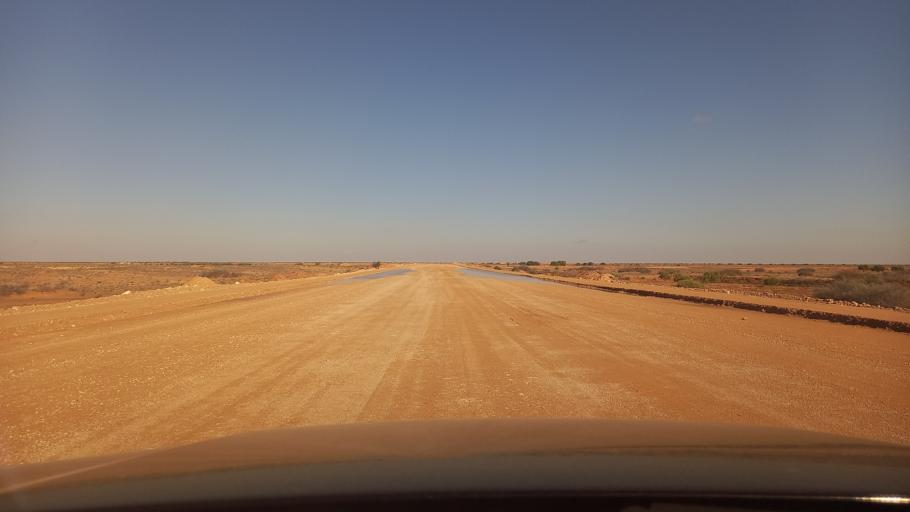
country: TN
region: Tataouine
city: Tataouine
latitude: 33.1372
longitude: 10.5051
